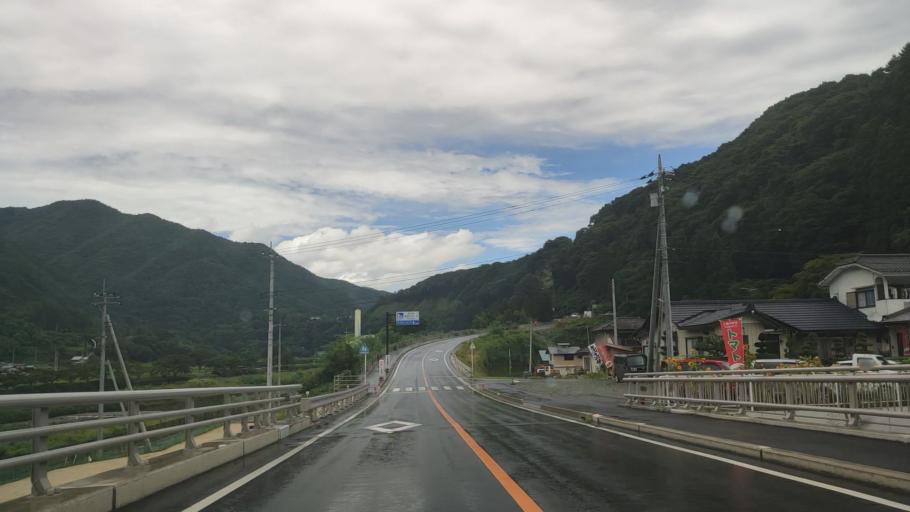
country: JP
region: Gunma
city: Numata
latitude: 36.7595
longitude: 139.2284
